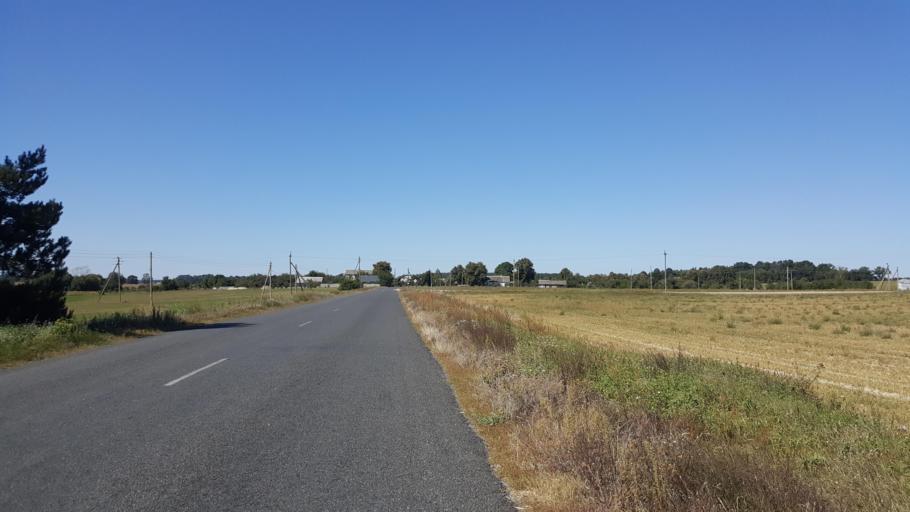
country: PL
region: Lublin Voivodeship
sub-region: Powiat bialski
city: Terespol
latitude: 52.2123
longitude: 23.5183
